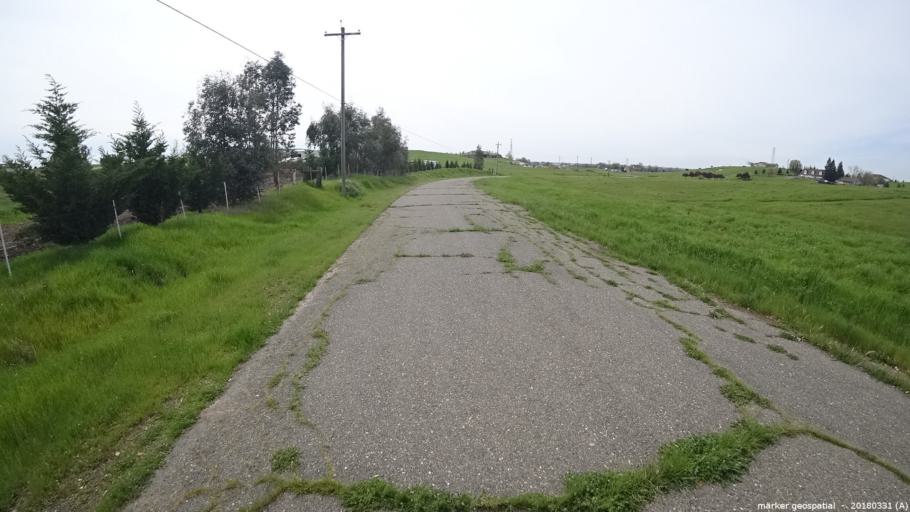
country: US
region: California
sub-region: Sacramento County
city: Rancho Murieta
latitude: 38.4942
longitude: -121.1369
